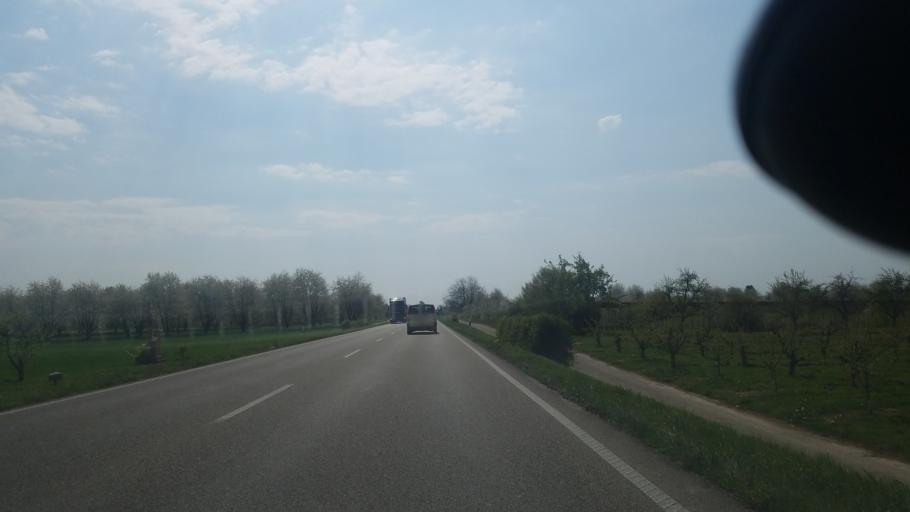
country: DE
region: Baden-Wuerttemberg
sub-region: Freiburg Region
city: Achern
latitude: 48.6143
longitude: 8.0416
